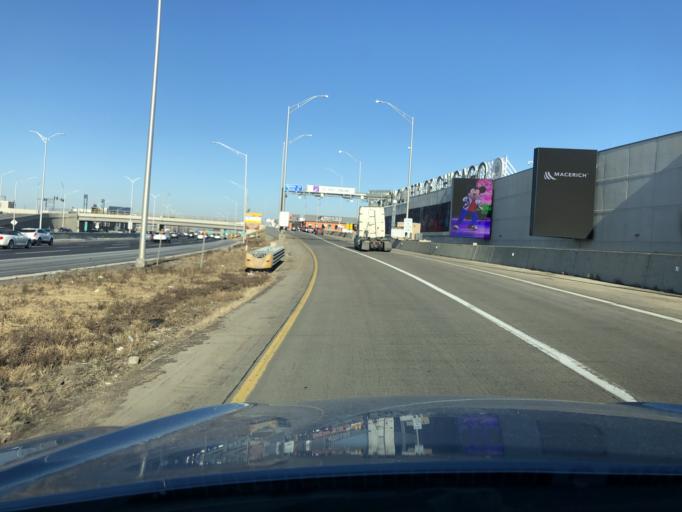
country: US
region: Illinois
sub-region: Cook County
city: Schiller Park
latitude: 41.9742
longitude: -87.8687
